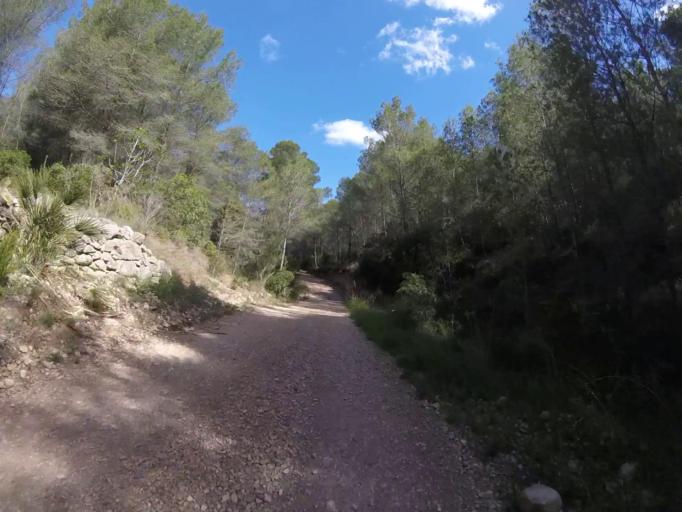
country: ES
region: Valencia
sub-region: Provincia de Castello
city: Alcoceber
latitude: 40.2966
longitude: 0.3143
